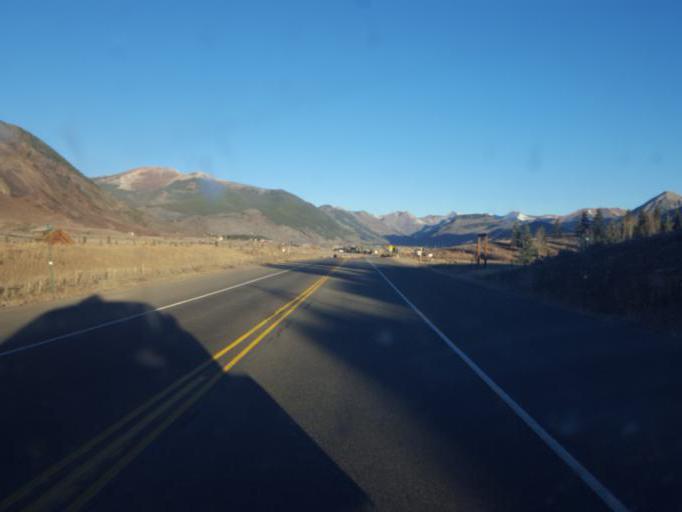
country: US
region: Colorado
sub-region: Gunnison County
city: Crested Butte
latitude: 38.8495
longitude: -106.9492
